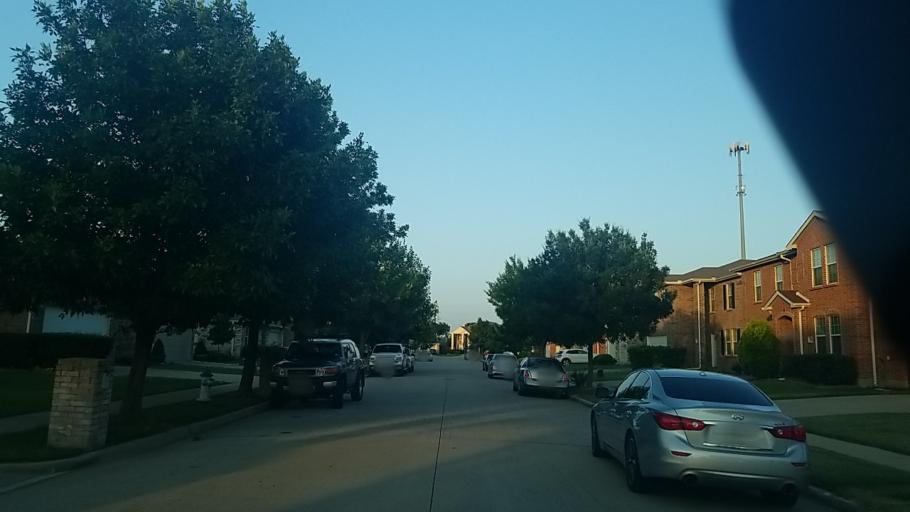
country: US
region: Texas
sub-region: Denton County
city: Corinth
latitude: 33.1508
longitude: -97.1047
